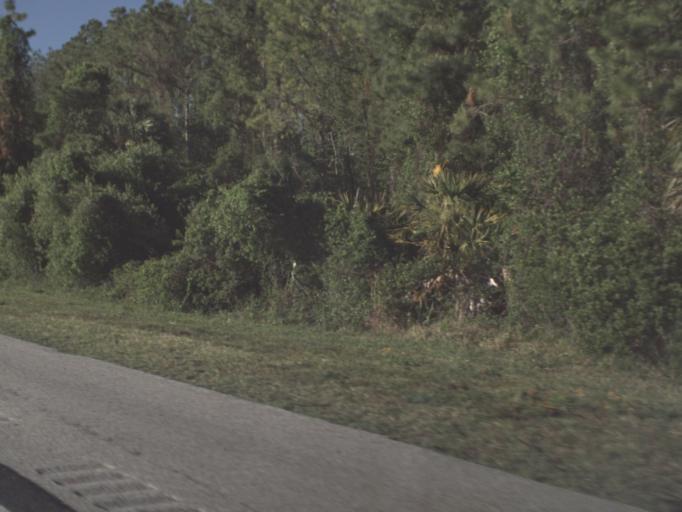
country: US
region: Florida
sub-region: Flagler County
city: Palm Coast
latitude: 29.6224
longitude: -81.2603
